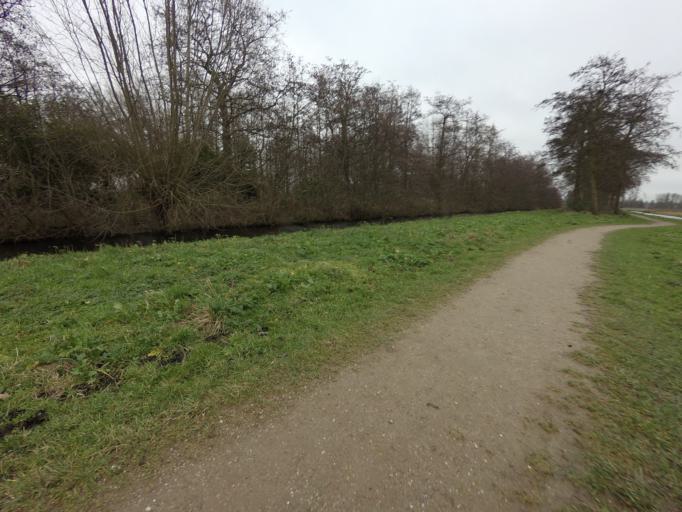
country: NL
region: South Holland
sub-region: Bodegraven-Reeuwijk
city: Reeuwijk
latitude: 52.0218
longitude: 4.7439
